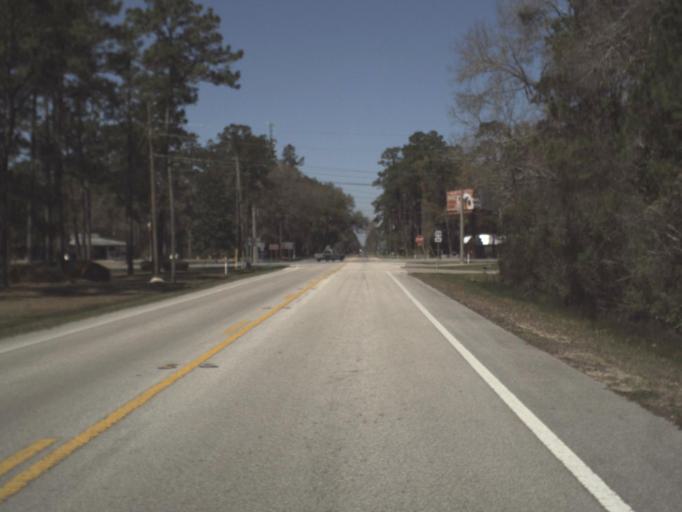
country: US
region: Florida
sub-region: Leon County
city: Woodville
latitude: 30.1893
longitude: -84.2152
